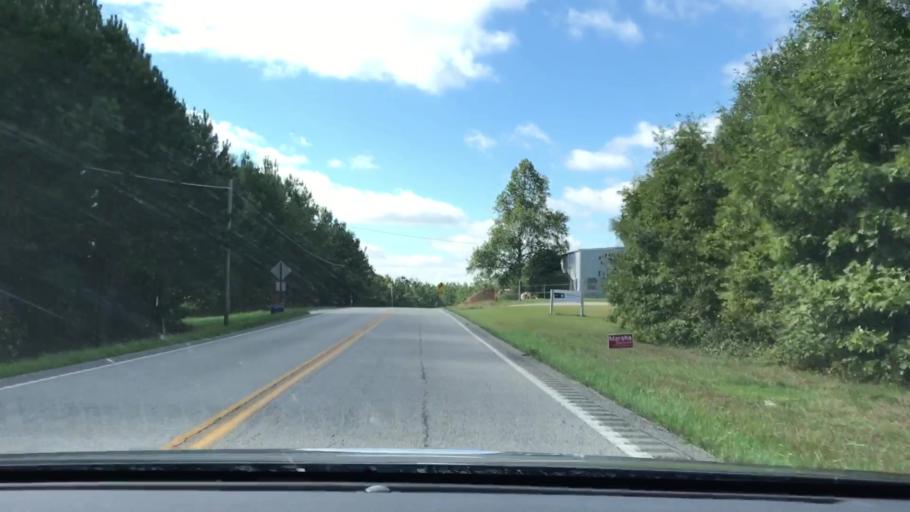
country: US
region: Tennessee
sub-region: Scott County
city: Huntsville
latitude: 36.3361
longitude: -84.6353
